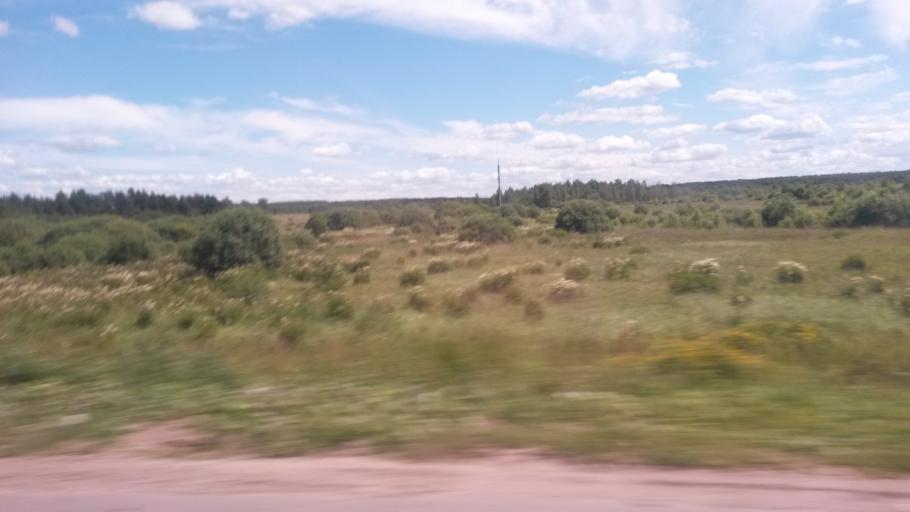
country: RU
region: Ivanovo
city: Rodniki
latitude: 57.1049
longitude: 41.7758
